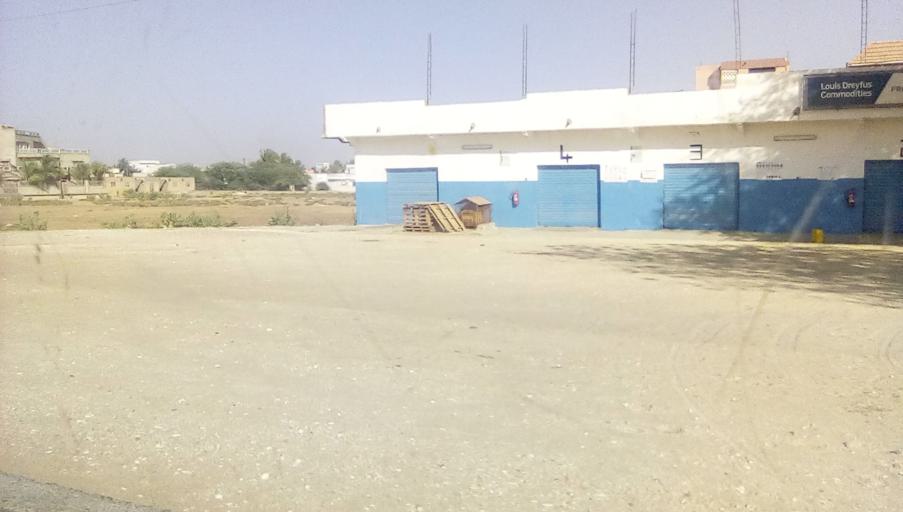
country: SN
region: Saint-Louis
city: Saint-Louis
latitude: 16.0451
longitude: -16.4369
